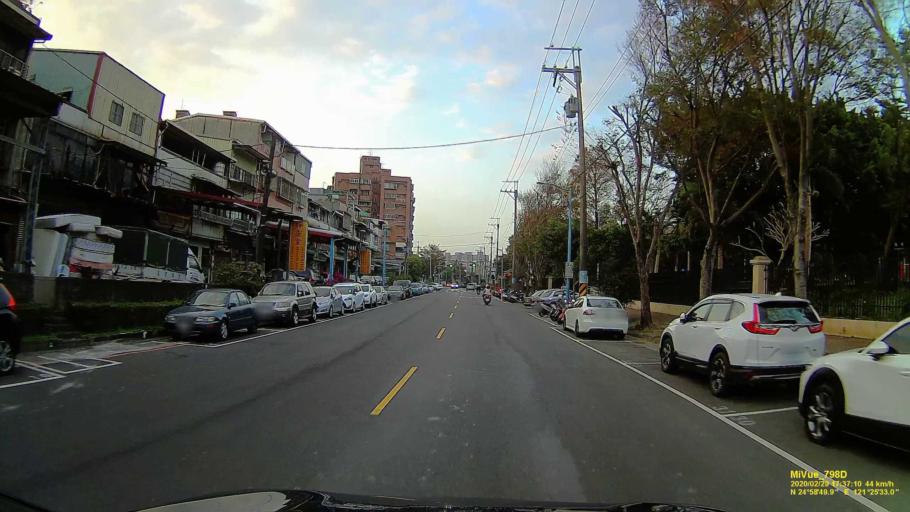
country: TW
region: Taipei
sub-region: Taipei
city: Banqiao
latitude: 24.9808
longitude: 121.4258
